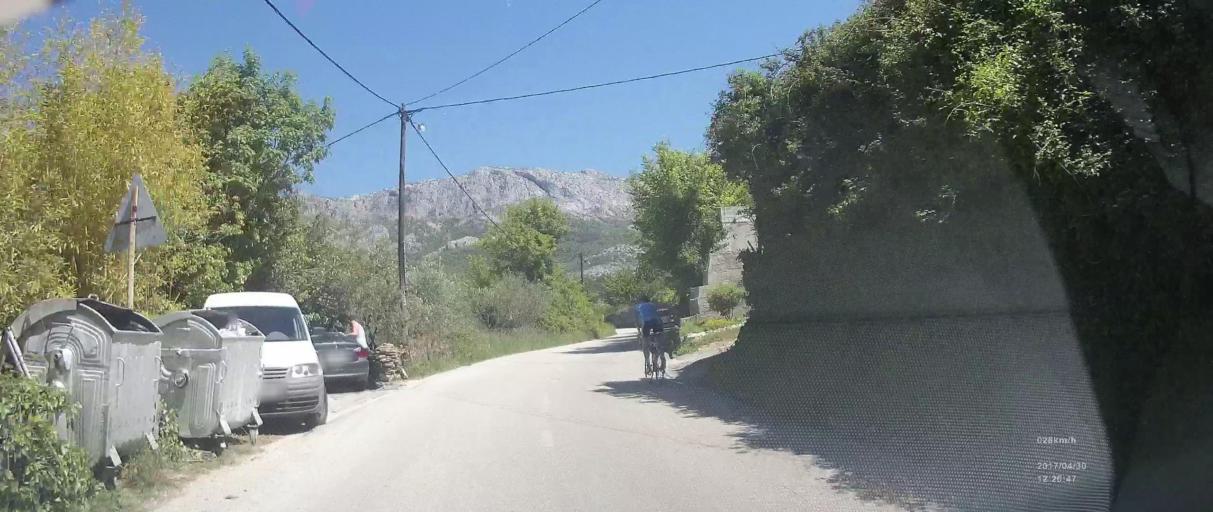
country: HR
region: Splitsko-Dalmatinska
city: Zrnovnica
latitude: 43.5185
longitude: 16.5587
